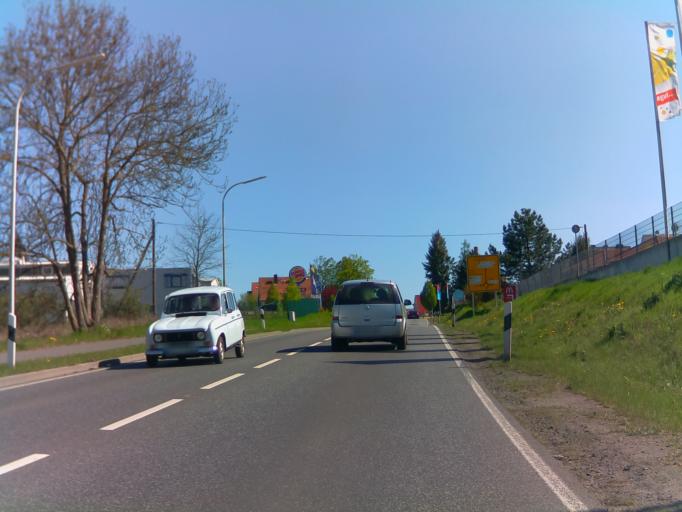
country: DE
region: Hesse
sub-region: Regierungsbezirk Giessen
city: Lauterbach
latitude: 50.6432
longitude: 9.3903
